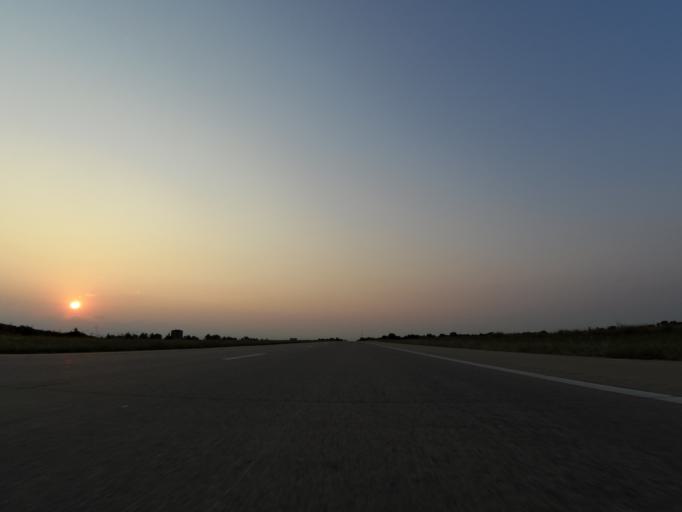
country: US
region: Kansas
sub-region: Reno County
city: Haven
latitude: 37.9258
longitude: -97.8413
